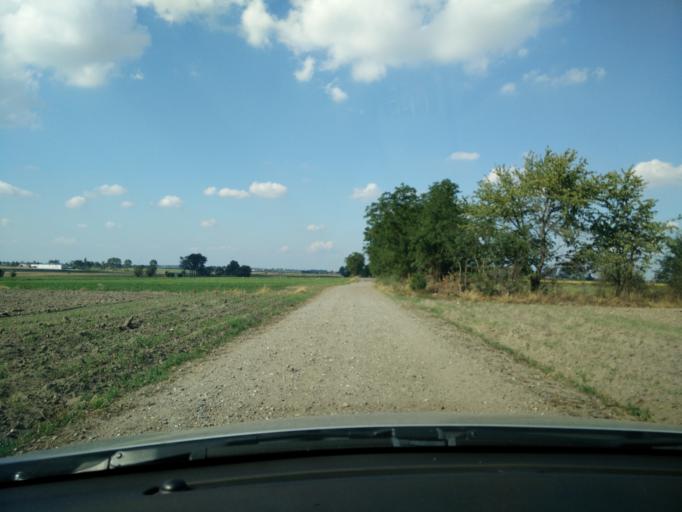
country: PL
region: Greater Poland Voivodeship
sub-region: Powiat poznanski
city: Kleszczewo
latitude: 52.2608
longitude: 17.1863
